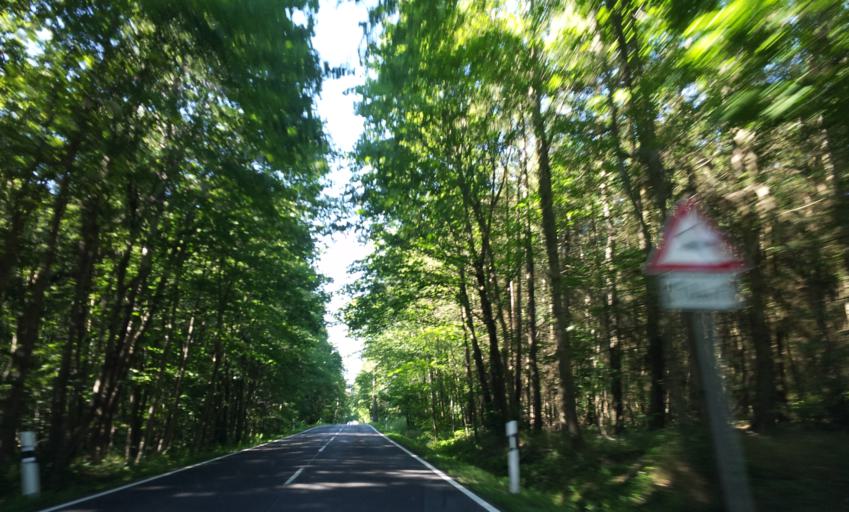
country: DE
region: Mecklenburg-Vorpommern
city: Gingst
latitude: 54.4222
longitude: 13.2800
